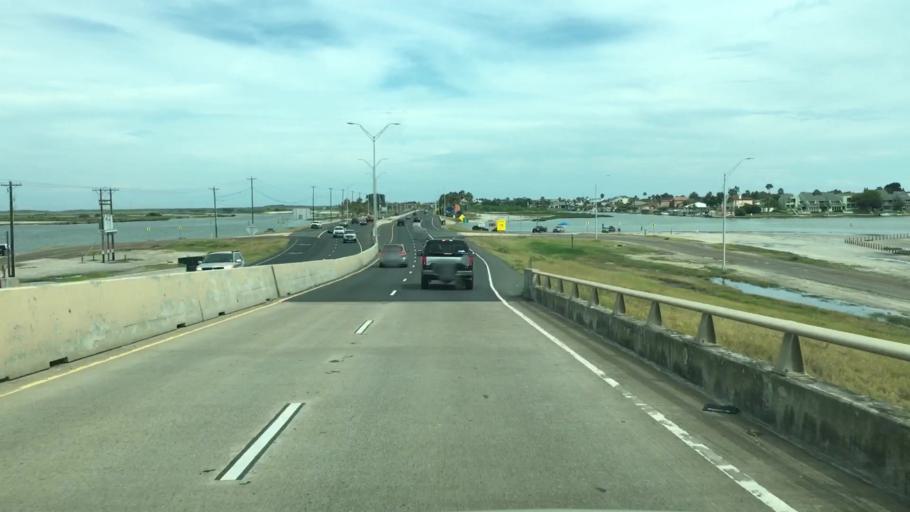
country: US
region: Texas
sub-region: Nueces County
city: Corpus Christi
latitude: 27.6328
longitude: -97.2355
